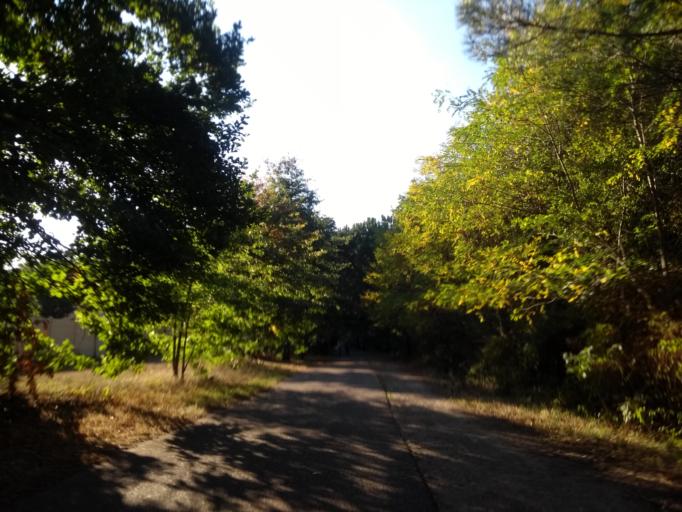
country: FR
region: Aquitaine
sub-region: Departement de la Gironde
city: Pessac
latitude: 44.8049
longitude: -0.6706
